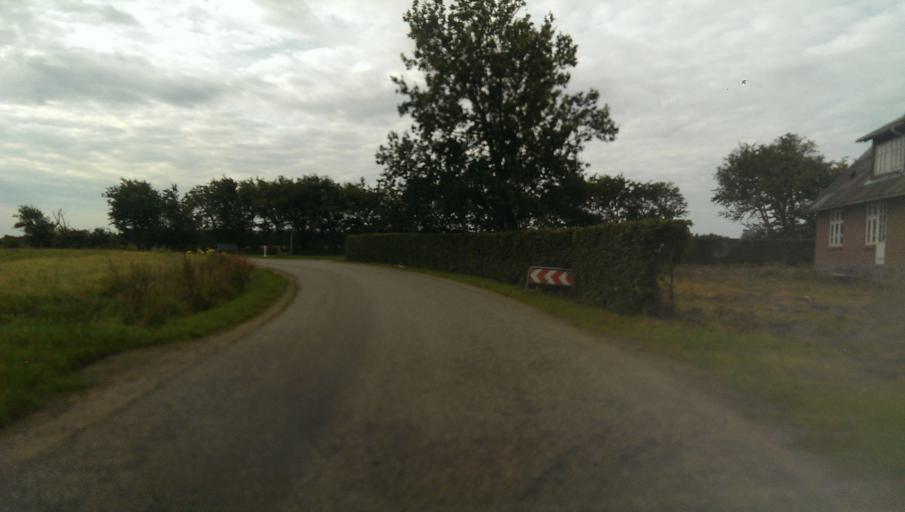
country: DK
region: South Denmark
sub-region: Esbjerg Kommune
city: Tjaereborg
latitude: 55.5139
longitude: 8.5247
